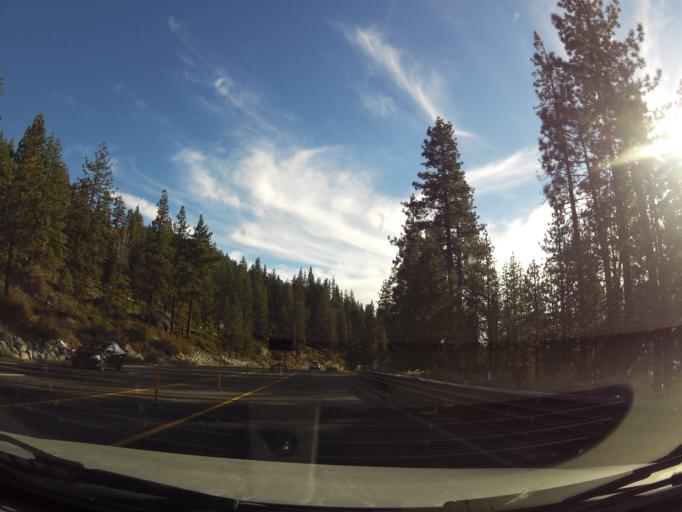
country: US
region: Nevada
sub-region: Douglas County
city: Kingsbury
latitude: 39.0722
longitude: -119.9406
